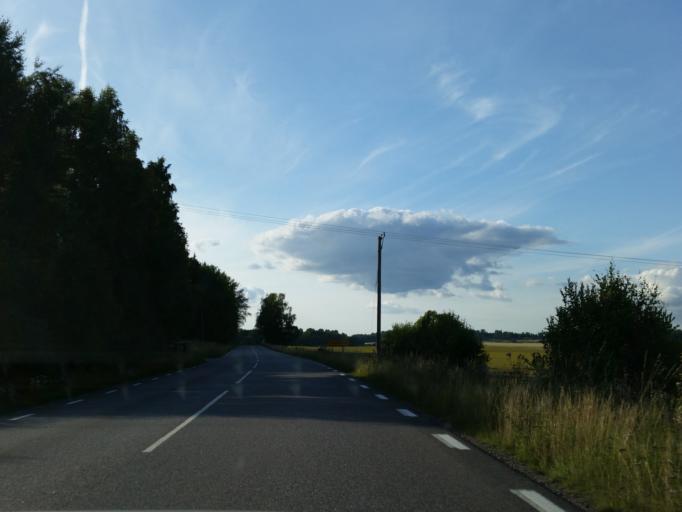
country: SE
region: Stockholm
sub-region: Sodertalje Kommun
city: Molnbo
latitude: 59.0114
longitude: 17.3758
